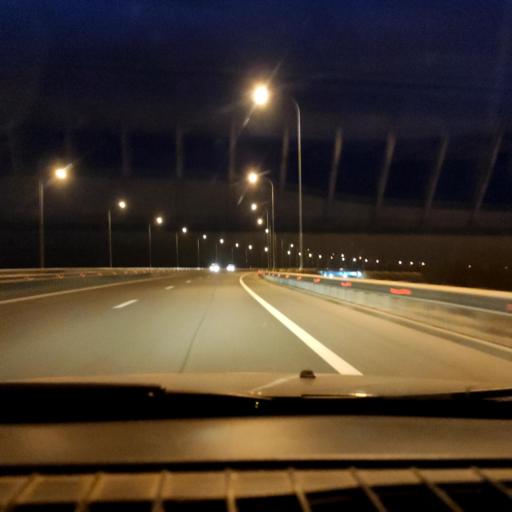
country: RU
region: Samara
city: Bereza
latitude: 53.4973
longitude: 50.1170
